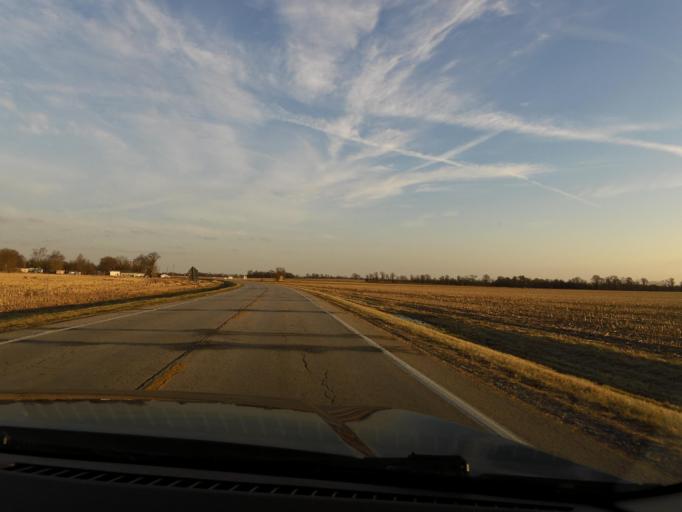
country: US
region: Illinois
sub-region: Fayette County
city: Vandalia
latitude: 38.8638
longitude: -89.0869
